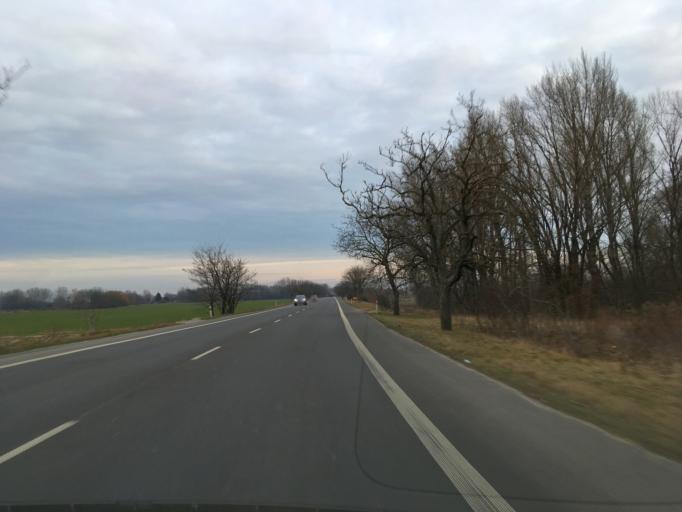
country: SK
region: Trnavsky
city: Dunajska Streda
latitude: 47.9734
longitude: 17.6704
